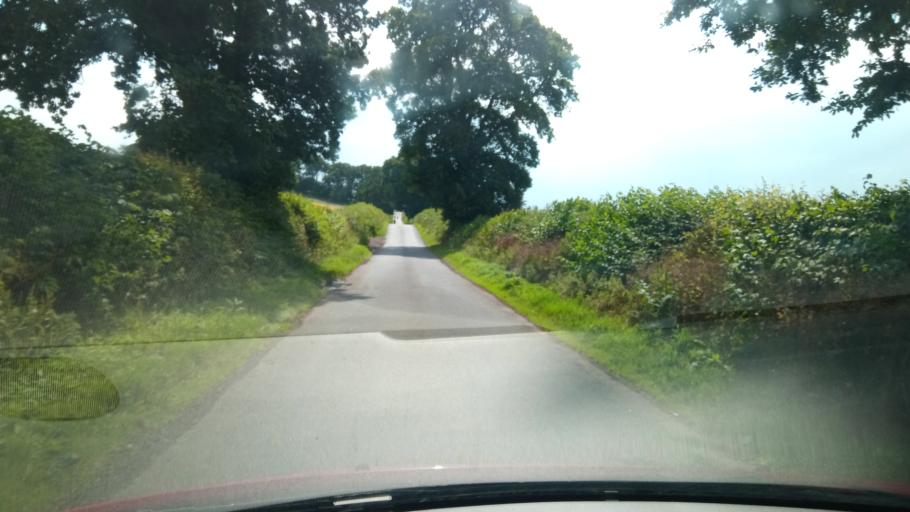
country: GB
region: Scotland
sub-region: The Scottish Borders
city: Kelso
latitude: 55.5862
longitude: -2.4715
